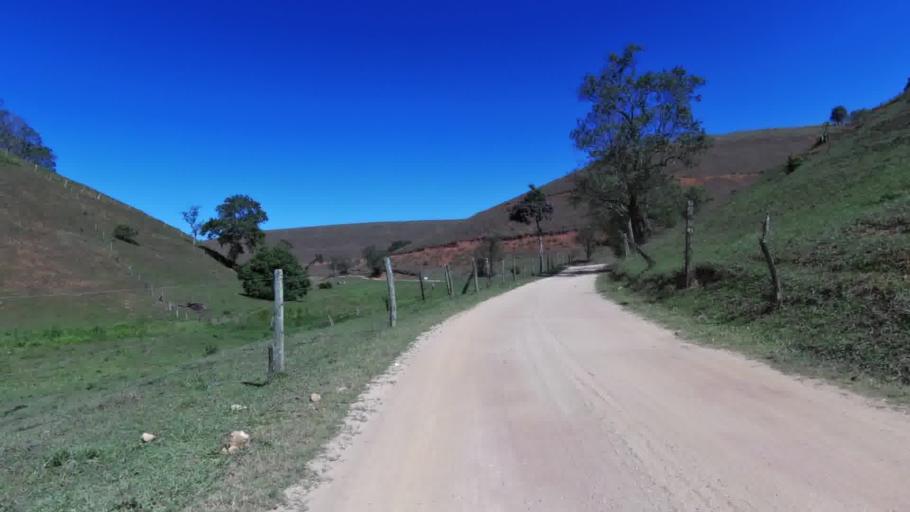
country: BR
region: Espirito Santo
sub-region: Rio Novo Do Sul
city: Rio Novo do Sul
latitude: -20.8710
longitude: -40.9335
